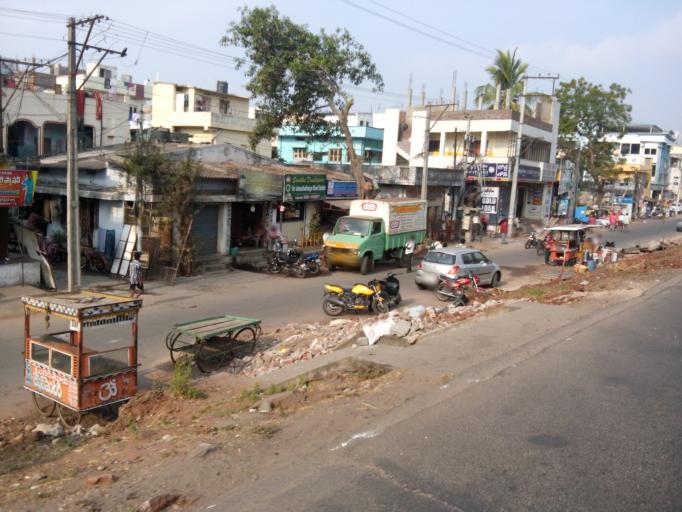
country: IN
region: Andhra Pradesh
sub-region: Krishna
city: Vijayawada
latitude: 16.5067
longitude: 80.6260
